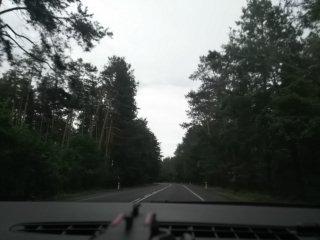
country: PL
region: Lublin Voivodeship
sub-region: Powiat janowski
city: Janow Lubelski
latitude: 50.6905
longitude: 22.3702
